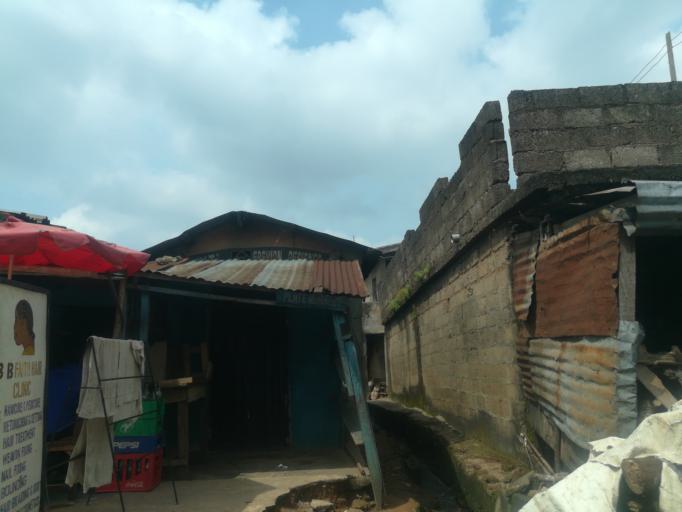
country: NG
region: Oyo
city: Ibadan
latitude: 7.4125
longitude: 3.9520
